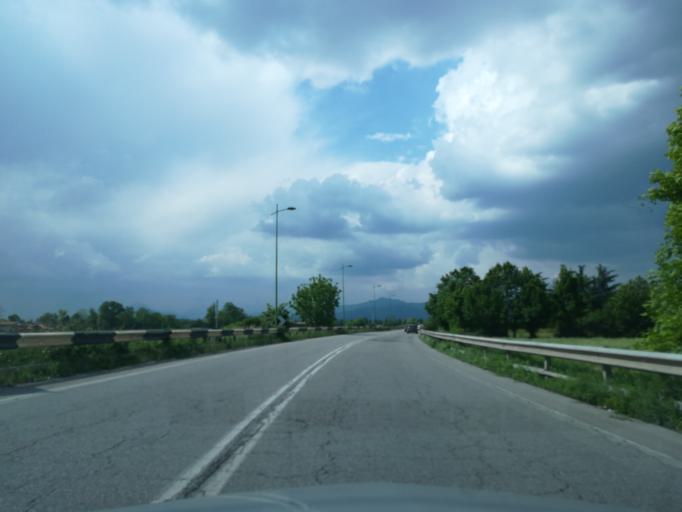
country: IT
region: Lombardy
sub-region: Provincia di Bergamo
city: Grassobbio
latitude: 45.6434
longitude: 9.7463
